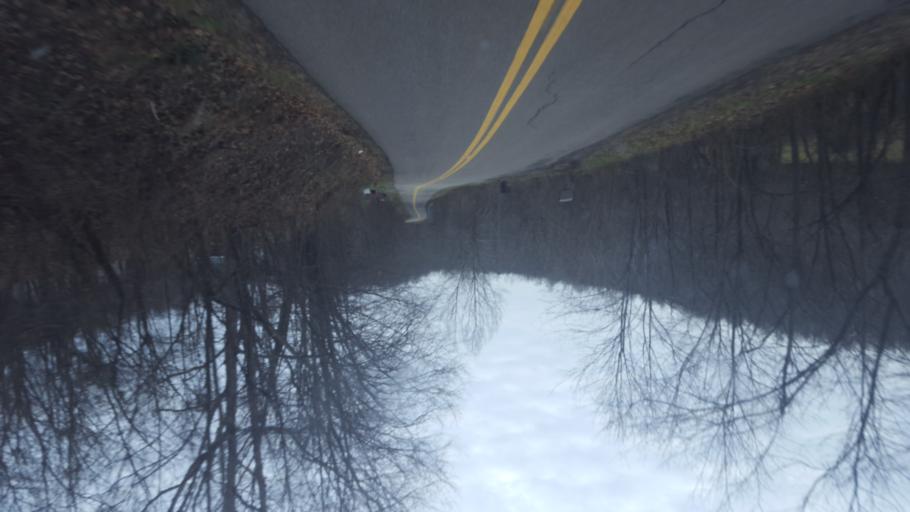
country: US
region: Ohio
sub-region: Gallia County
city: Gallipolis
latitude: 38.7190
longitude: -82.3273
